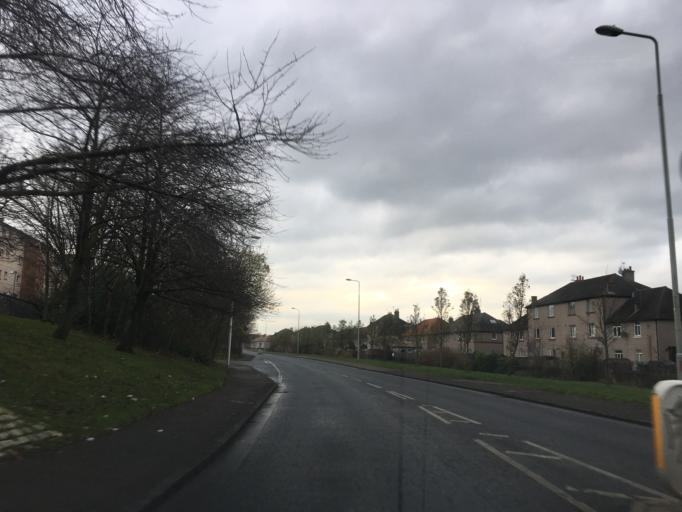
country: GB
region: Scotland
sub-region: Edinburgh
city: Colinton
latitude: 55.9211
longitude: -3.2779
